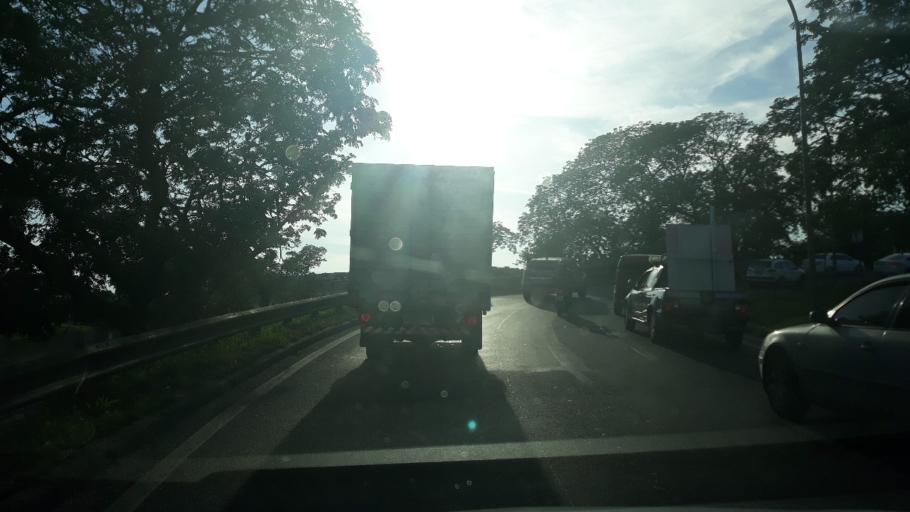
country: BR
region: Rio de Janeiro
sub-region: Rio De Janeiro
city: Rio de Janeiro
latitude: -22.8698
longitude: -43.2458
